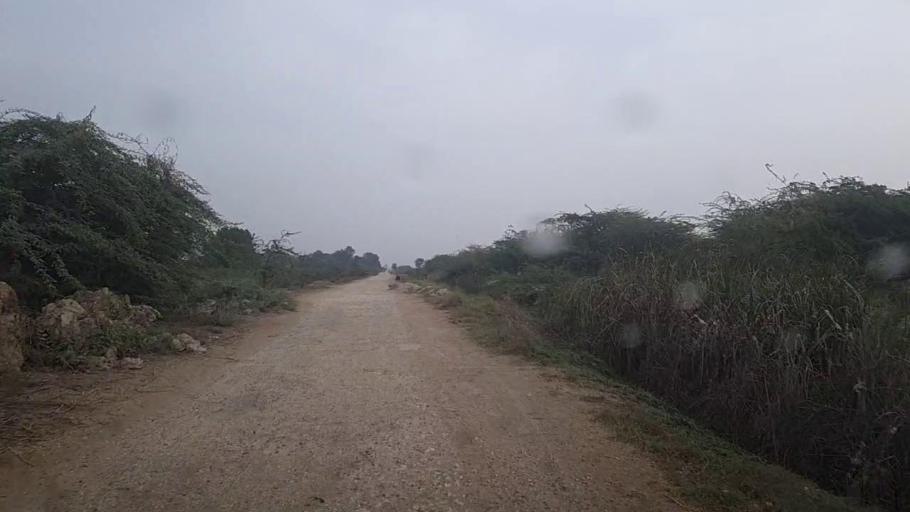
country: PK
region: Sindh
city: Gambat
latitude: 27.3748
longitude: 68.5703
